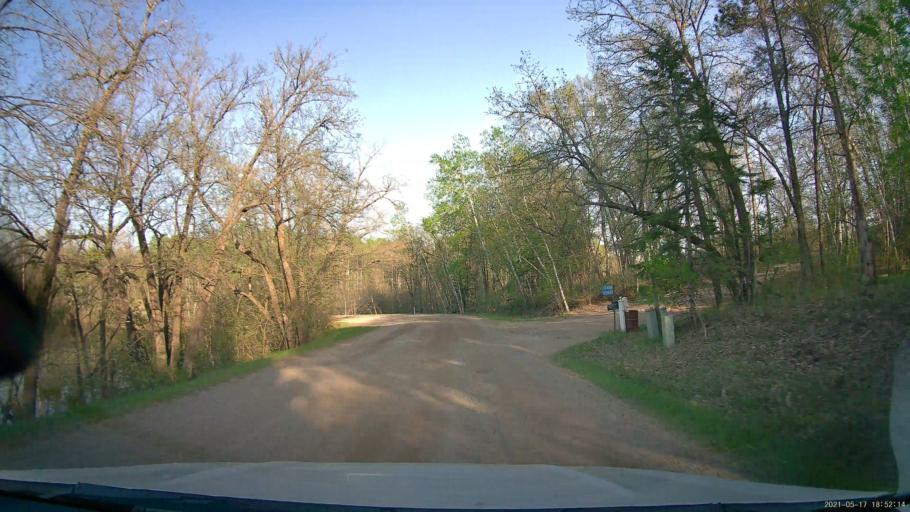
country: US
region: Minnesota
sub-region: Hubbard County
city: Park Rapids
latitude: 46.9435
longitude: -95.0026
